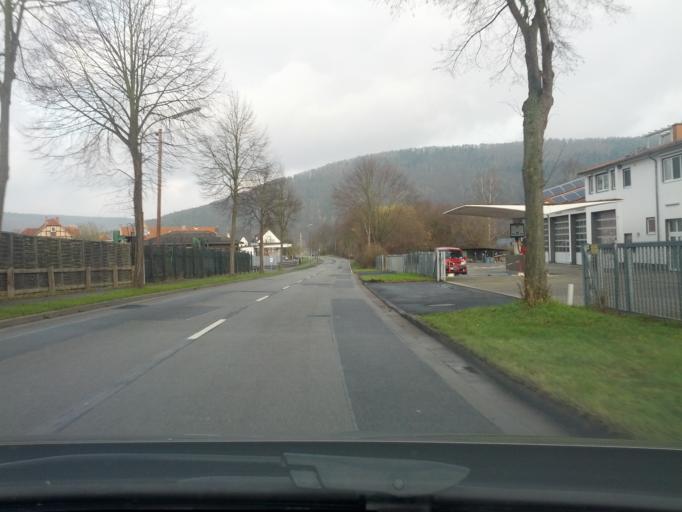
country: DE
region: Lower Saxony
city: Buhren
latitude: 51.4980
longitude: 9.6008
